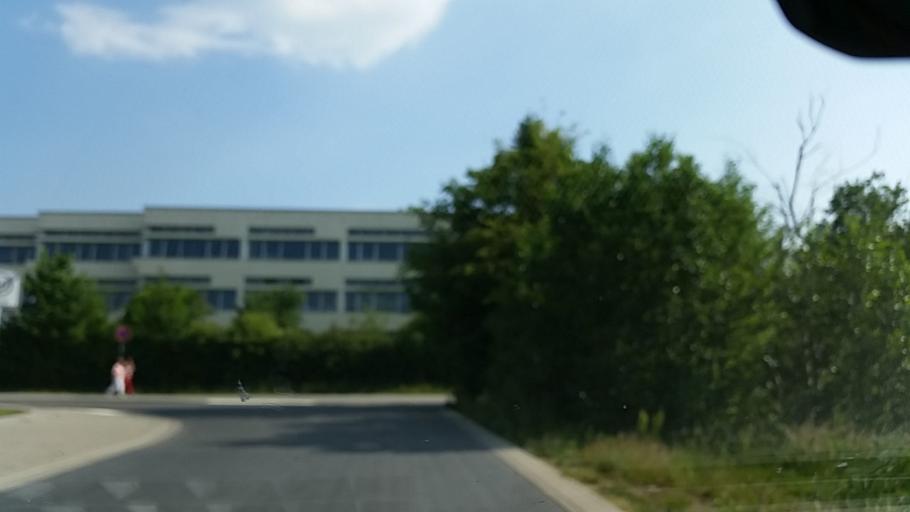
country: DE
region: Lower Saxony
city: Wolfsburg
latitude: 52.4043
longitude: 10.7482
